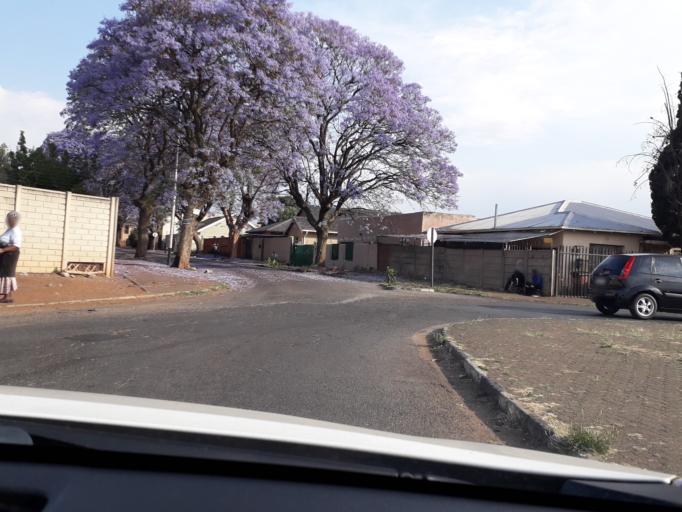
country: ZA
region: Gauteng
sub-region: City of Johannesburg Metropolitan Municipality
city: Johannesburg
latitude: -26.1747
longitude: 27.9674
